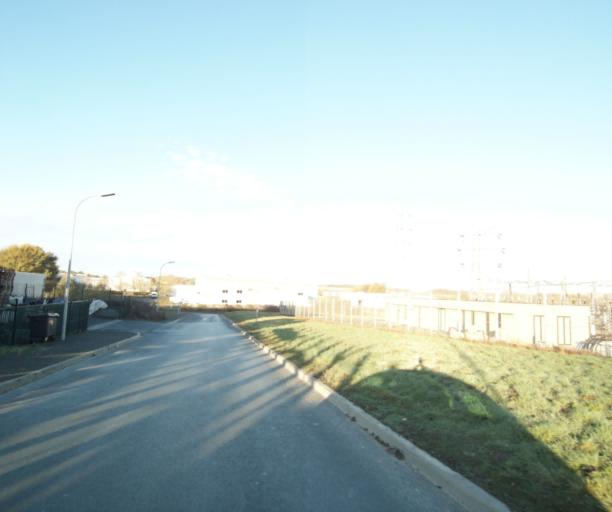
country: FR
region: Poitou-Charentes
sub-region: Departement de la Charente-Maritime
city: Saintes
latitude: 45.7514
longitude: -0.6656
